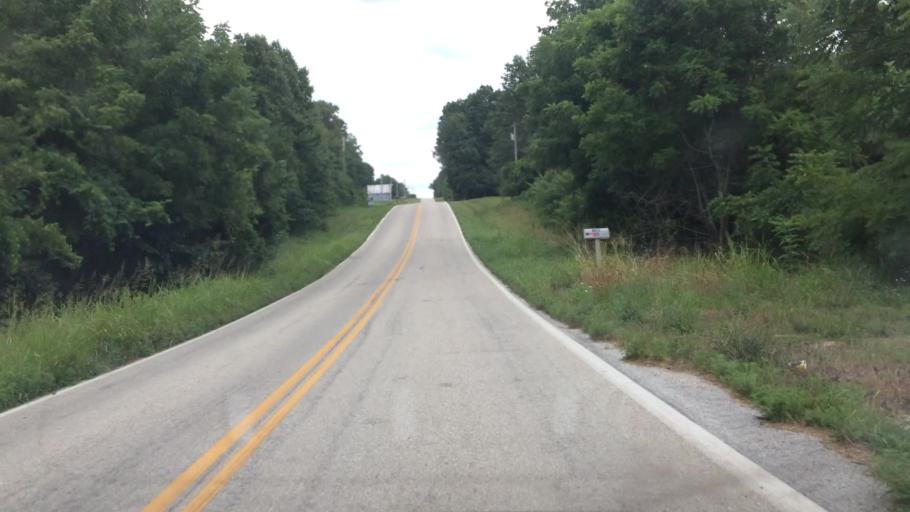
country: US
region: Missouri
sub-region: Greene County
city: Strafford
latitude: 37.3004
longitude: -93.1592
